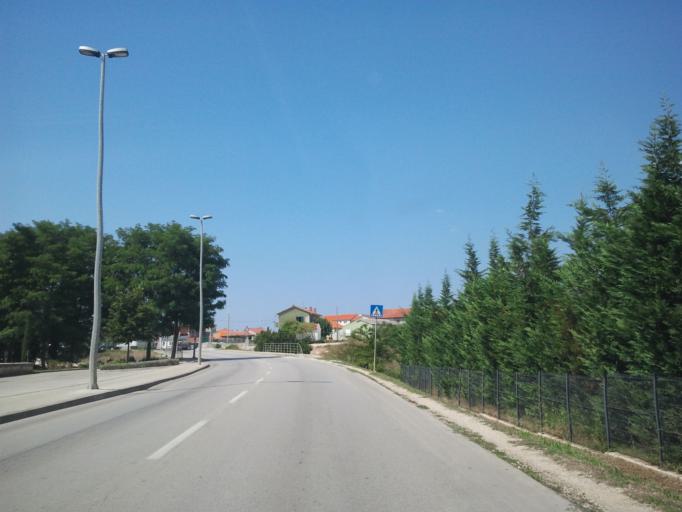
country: HR
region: Zadarska
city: Zadar
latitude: 44.1053
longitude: 15.2573
